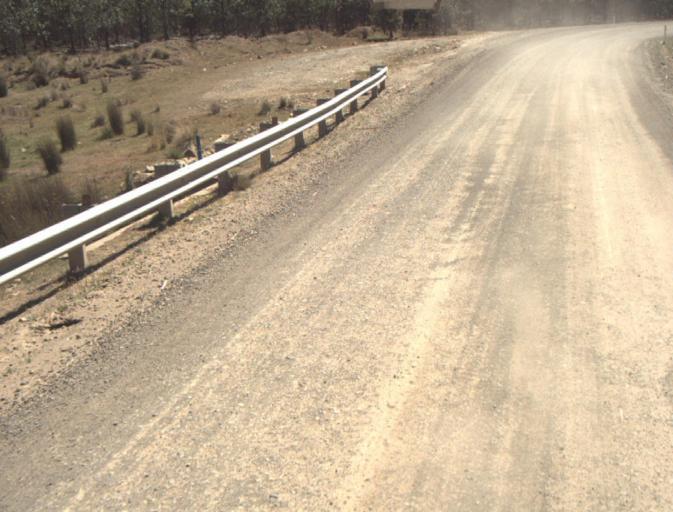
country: AU
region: Tasmania
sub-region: Dorset
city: Scottsdale
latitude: -41.3708
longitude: 147.4716
